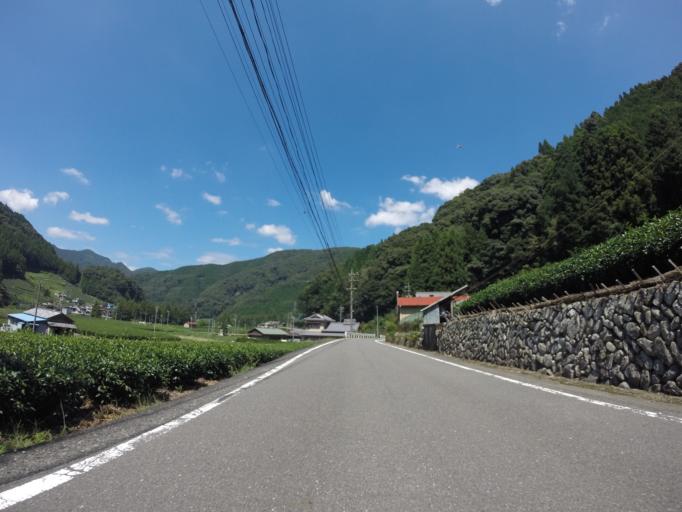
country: JP
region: Shizuoka
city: Shizuoka-shi
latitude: 35.0432
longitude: 138.2510
